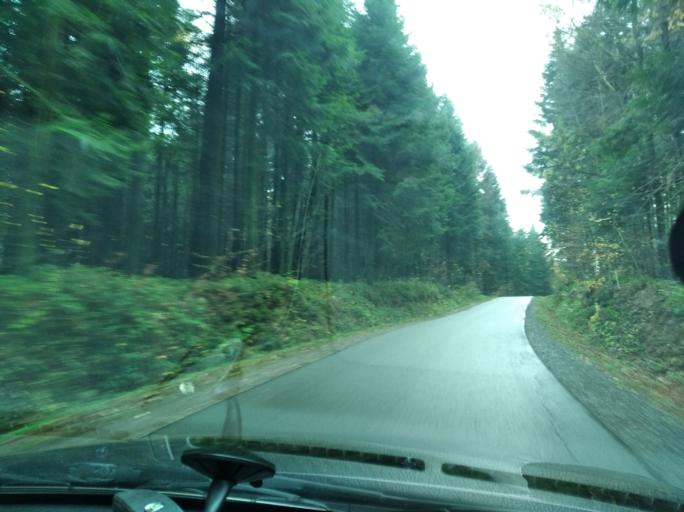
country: PL
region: Subcarpathian Voivodeship
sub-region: Powiat strzyzowski
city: Strzyzow
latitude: 49.9044
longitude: 21.7845
